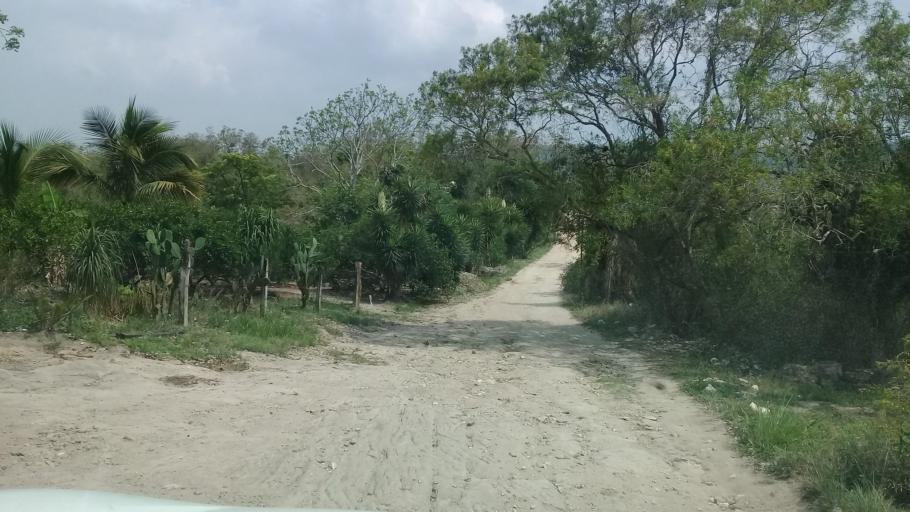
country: MX
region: Veracruz
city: Jalcomulco
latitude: 19.3873
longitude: -96.7913
